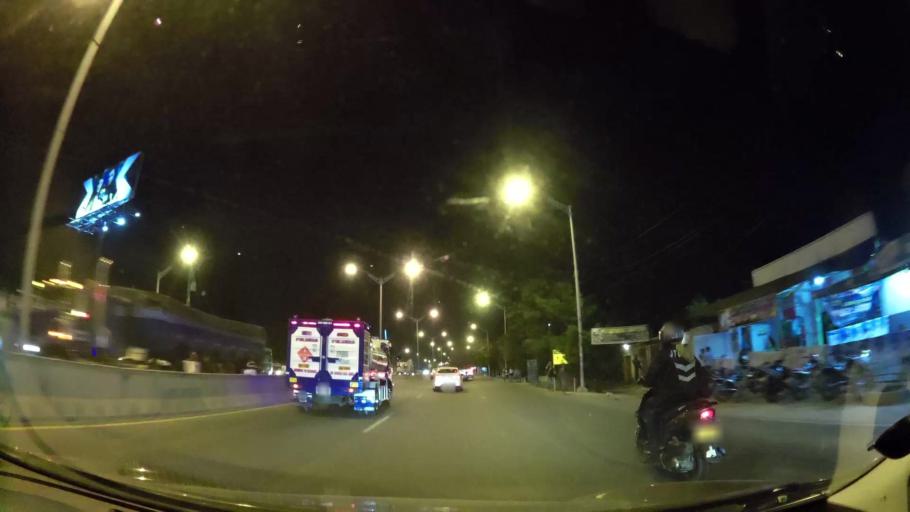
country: CO
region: Atlantico
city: Barranquilla
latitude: 10.9686
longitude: -74.8380
